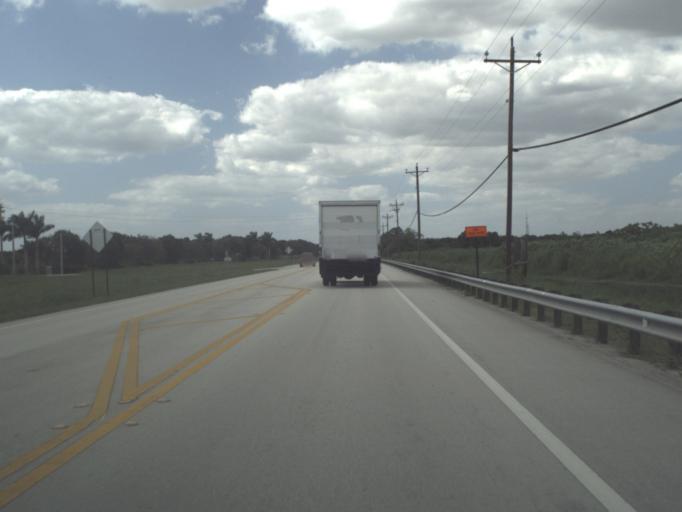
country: US
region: Florida
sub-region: Collier County
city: Lely Resort
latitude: 26.0145
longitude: -81.6229
